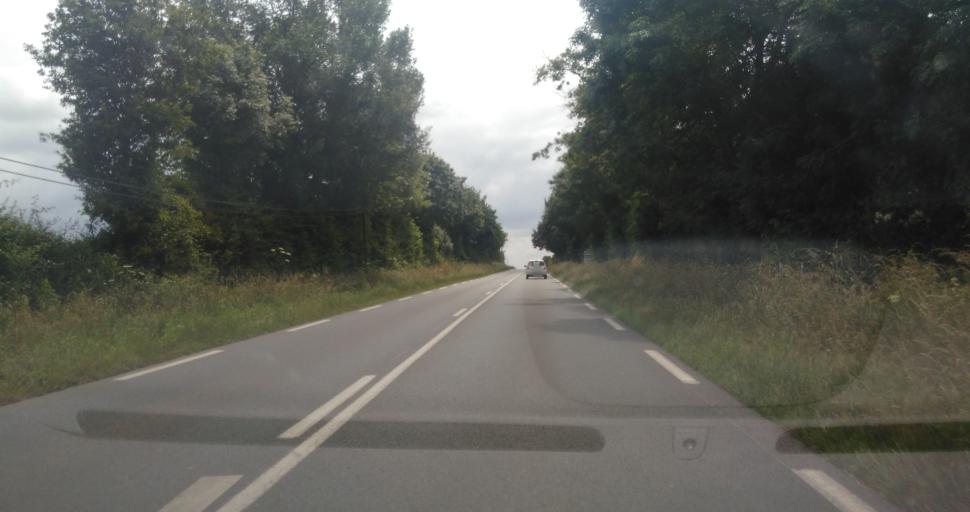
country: FR
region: Pays de la Loire
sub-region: Departement de la Vendee
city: Bournezeau
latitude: 46.6237
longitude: -1.1575
